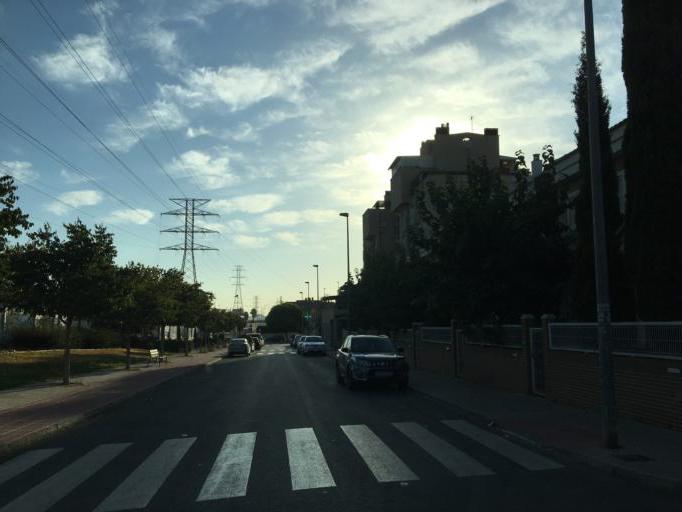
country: ES
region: Murcia
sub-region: Murcia
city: Murcia
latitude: 38.0161
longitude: -1.1629
